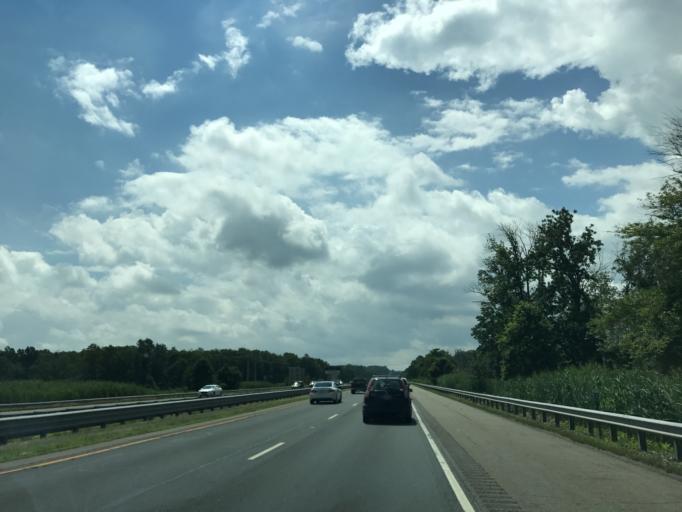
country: US
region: New Jersey
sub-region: Morris County
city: Madison
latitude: 40.7859
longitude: -74.4200
